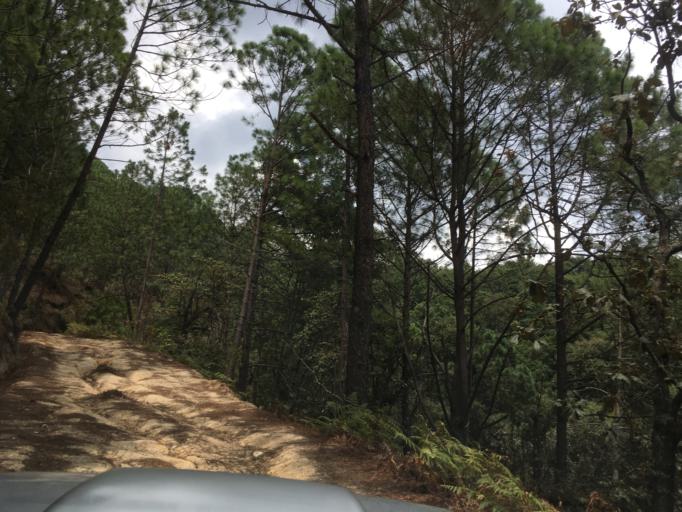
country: MX
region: Michoacan
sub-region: Zitacuaro
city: Macutzio
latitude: 19.5032
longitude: -100.3304
